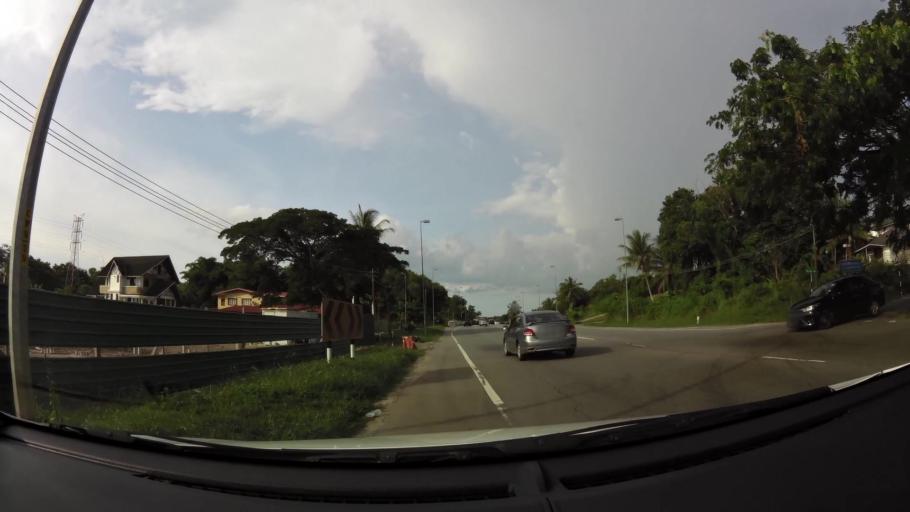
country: BN
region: Brunei and Muara
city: Bandar Seri Begawan
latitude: 4.9700
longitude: 114.9787
